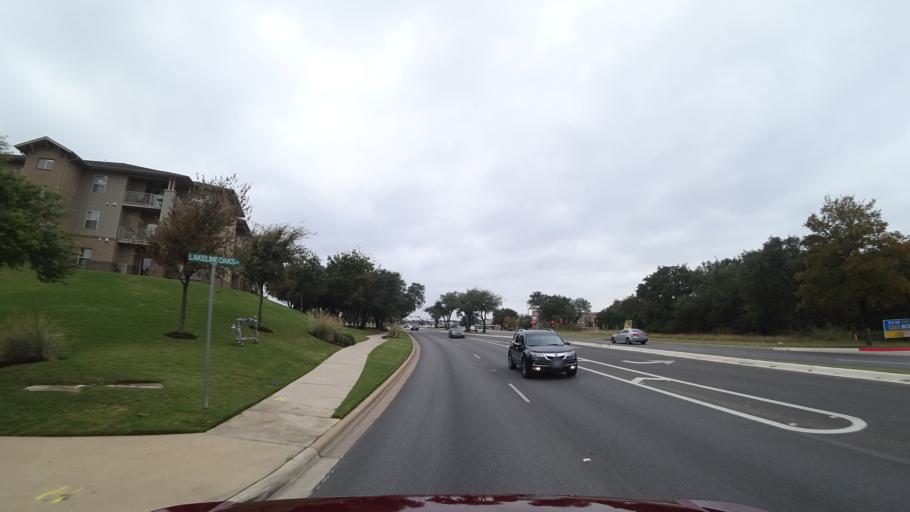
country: US
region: Texas
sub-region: Williamson County
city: Cedar Park
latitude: 30.4812
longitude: -97.8260
